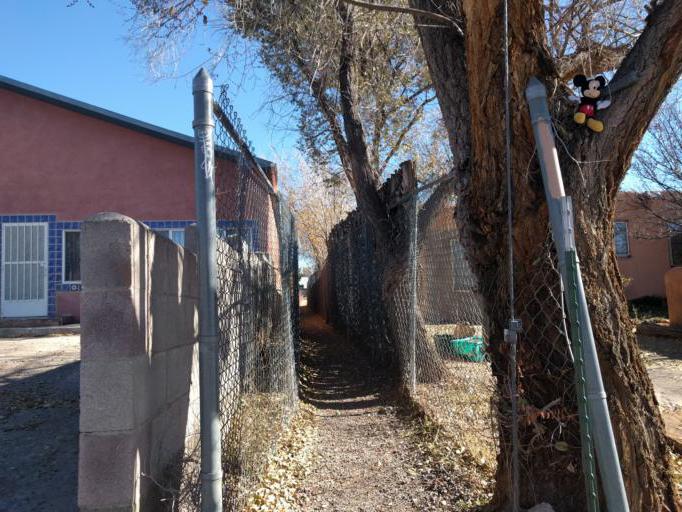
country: US
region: New Mexico
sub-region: Santa Fe County
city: Santa Fe
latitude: 35.6679
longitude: -105.9615
